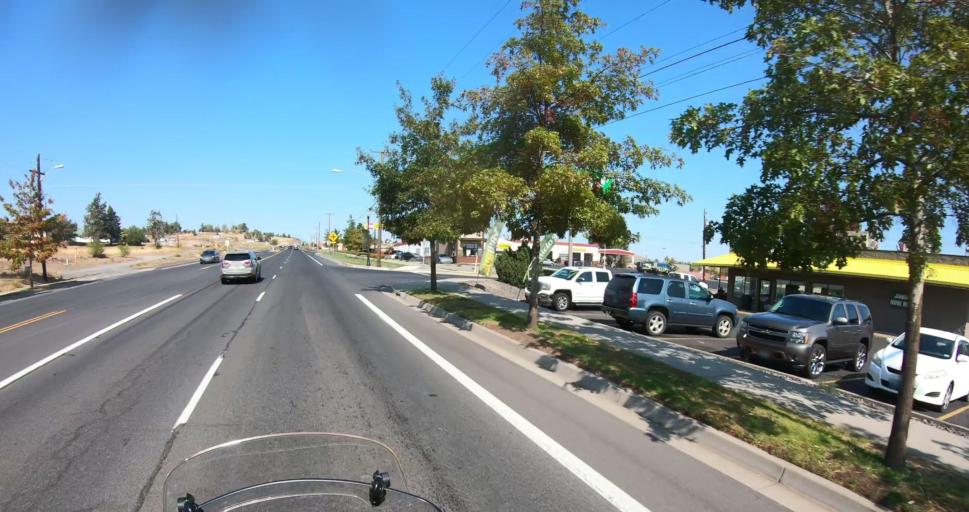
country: US
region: Oregon
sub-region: Jefferson County
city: Madras
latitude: 44.6419
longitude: -121.1321
